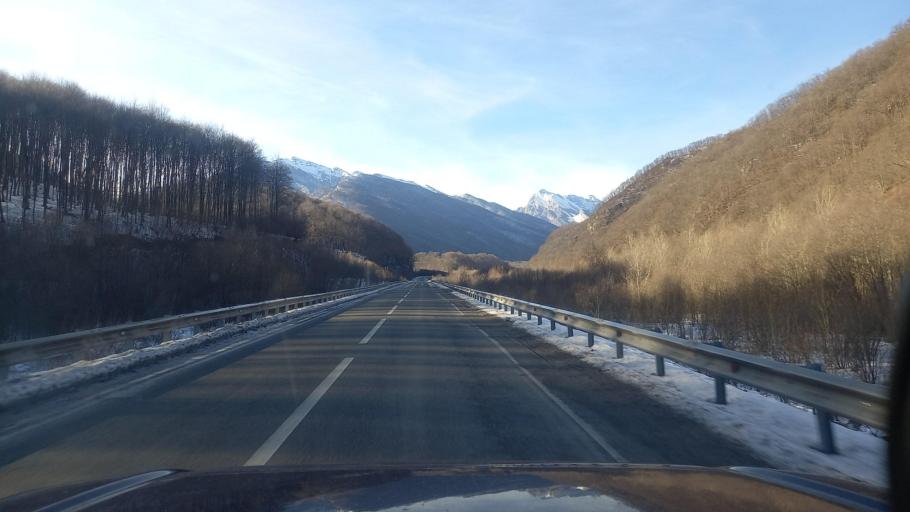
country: RU
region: North Ossetia
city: Gizel'
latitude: 42.9360
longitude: 44.5556
